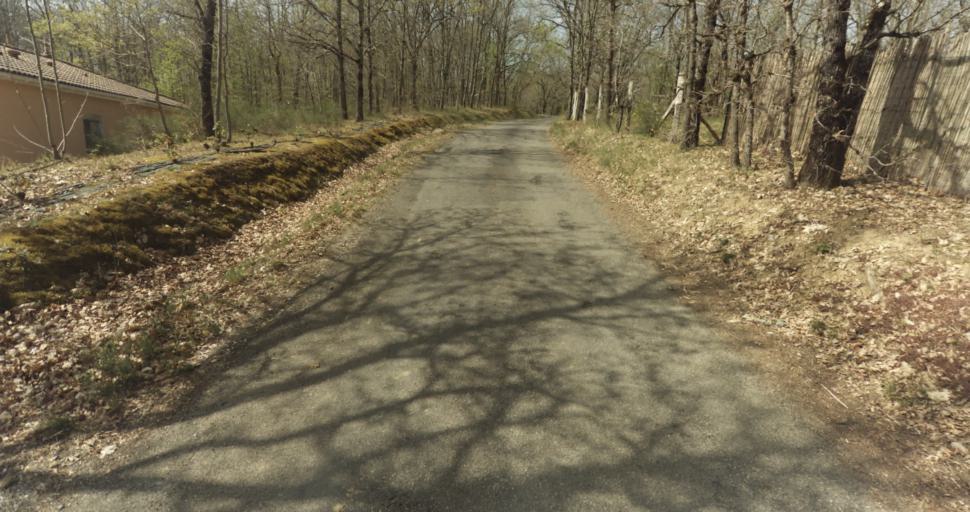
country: FR
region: Midi-Pyrenees
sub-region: Departement du Tarn-et-Garonne
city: Moissac
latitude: 44.1388
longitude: 1.0963
